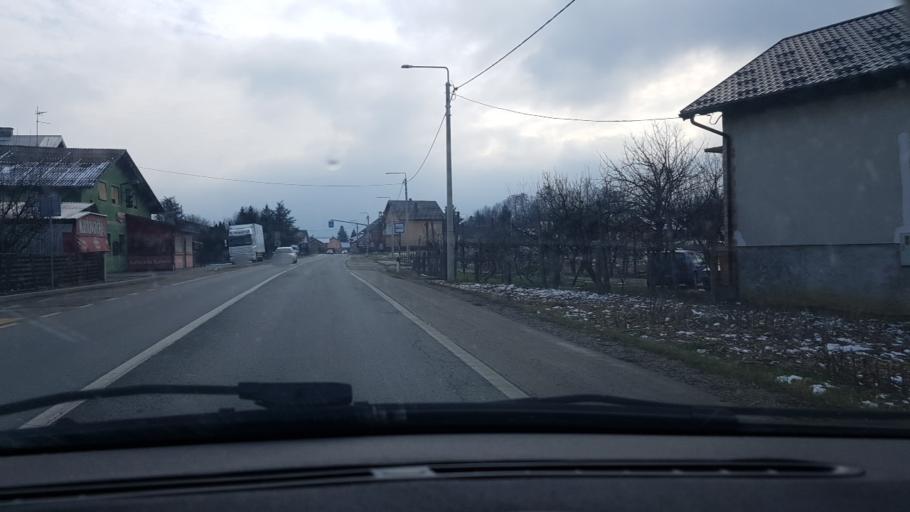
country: HR
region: Varazdinska
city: Tuzno
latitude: 46.2785
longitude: 16.2067
